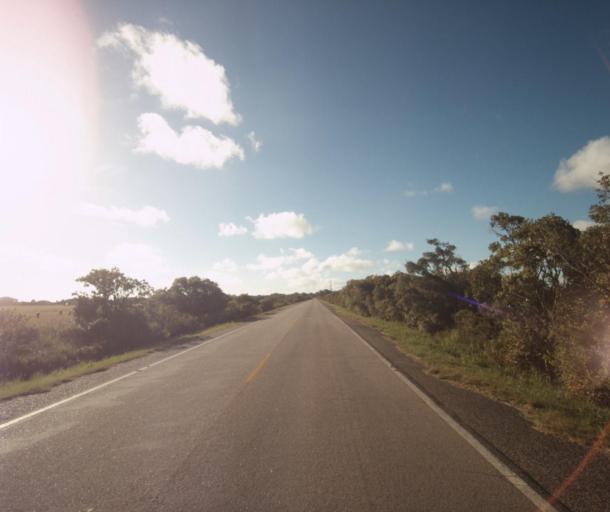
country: BR
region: Rio Grande do Sul
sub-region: Arroio Grande
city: Arroio Grande
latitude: -32.5068
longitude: -52.5678
